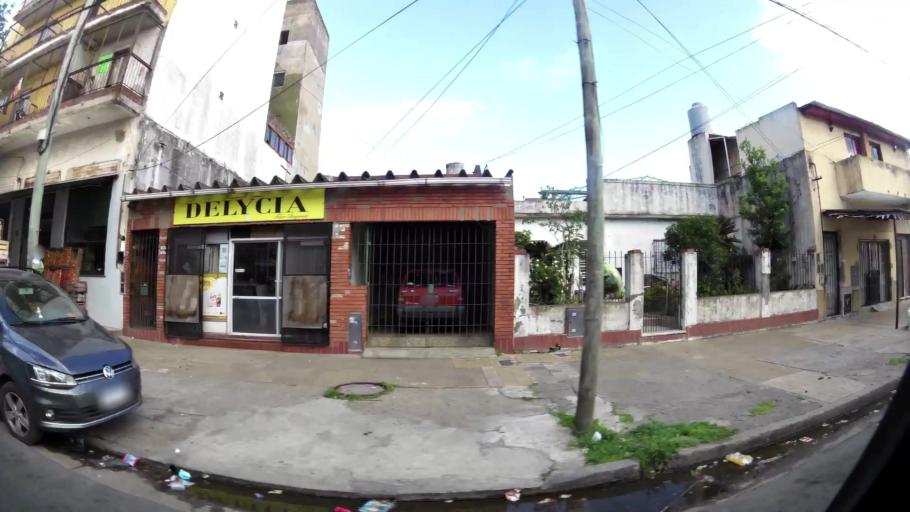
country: AR
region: Buenos Aires
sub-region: Partido de Avellaneda
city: Avellaneda
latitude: -34.6821
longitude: -58.3582
